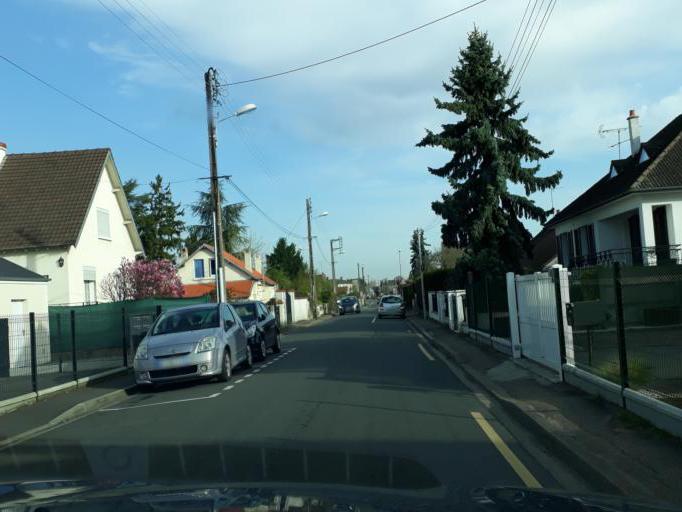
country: FR
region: Centre
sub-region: Departement du Loiret
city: La Chapelle-Saint-Mesmin
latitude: 47.8940
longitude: 1.8462
